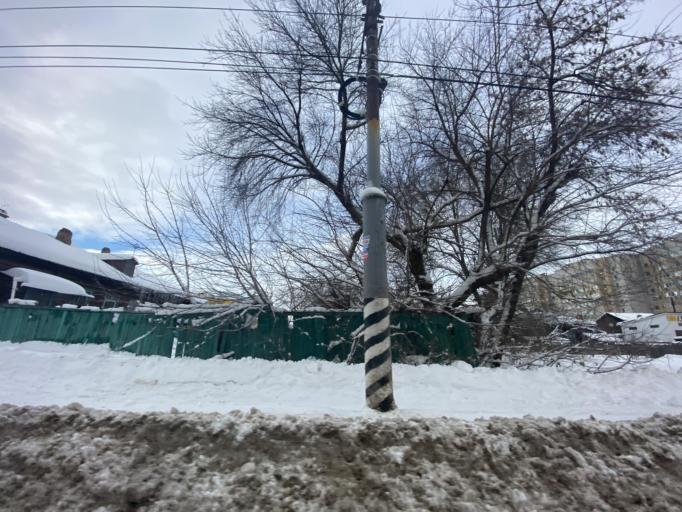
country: RU
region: Saratov
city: Engel's
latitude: 51.4971
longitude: 46.0943
